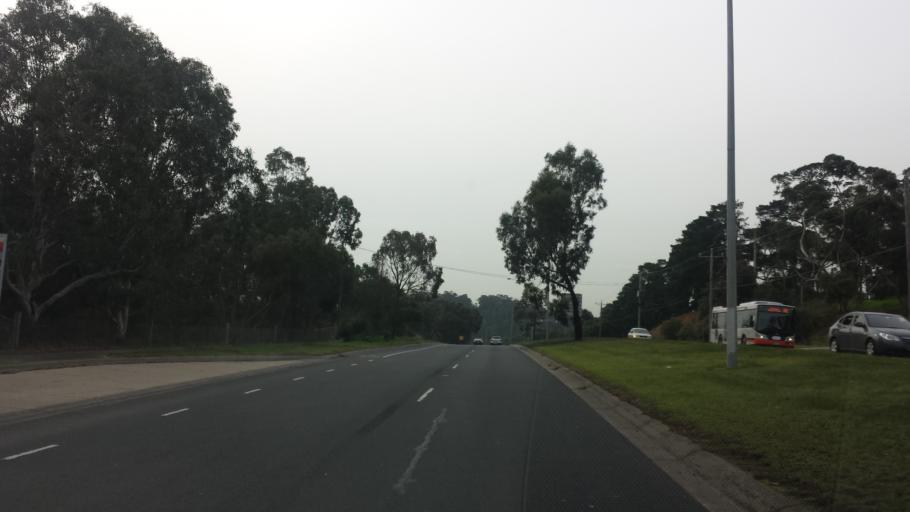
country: AU
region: Victoria
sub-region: Nillumbik
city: Eltham
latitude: -37.7459
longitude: 145.1361
